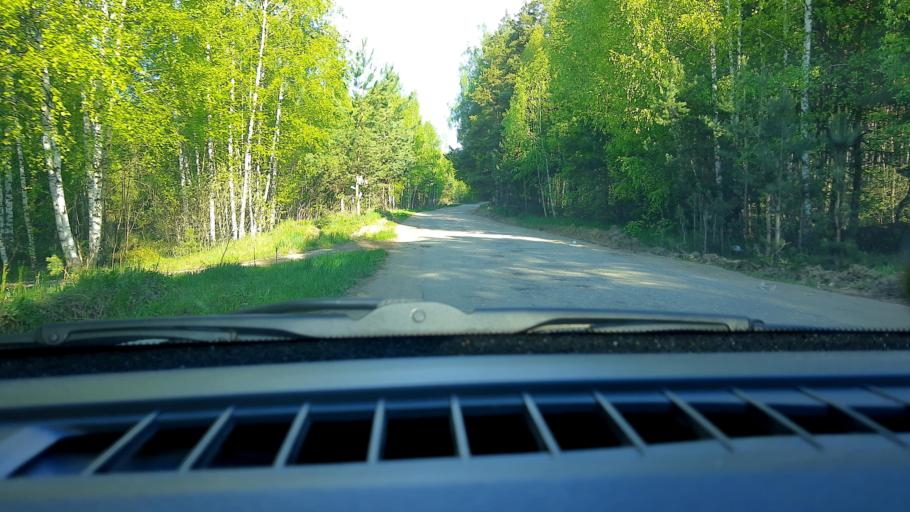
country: RU
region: Nizjnij Novgorod
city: Sitniki
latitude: 56.4142
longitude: 44.0539
